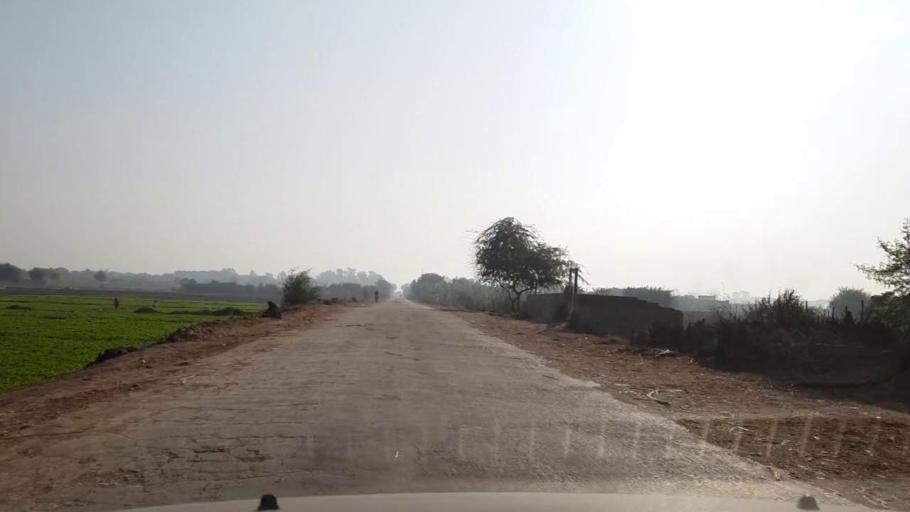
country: PK
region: Sindh
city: Matiari
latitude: 25.5829
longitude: 68.4909
